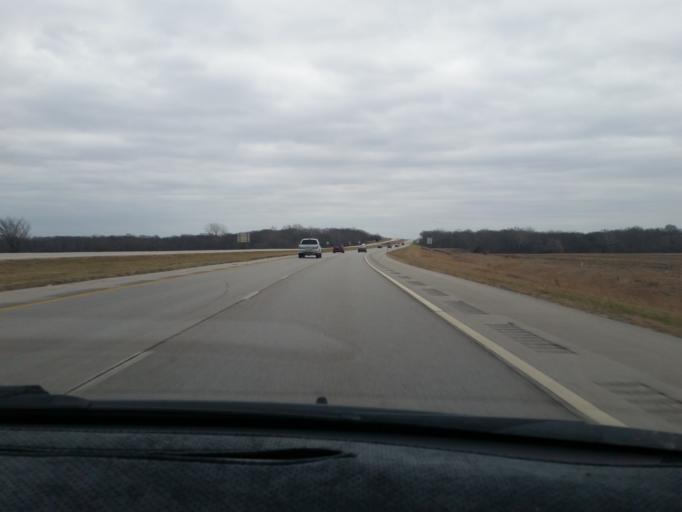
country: US
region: Kansas
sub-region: Douglas County
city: Eudora
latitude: 38.9348
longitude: -95.1402
